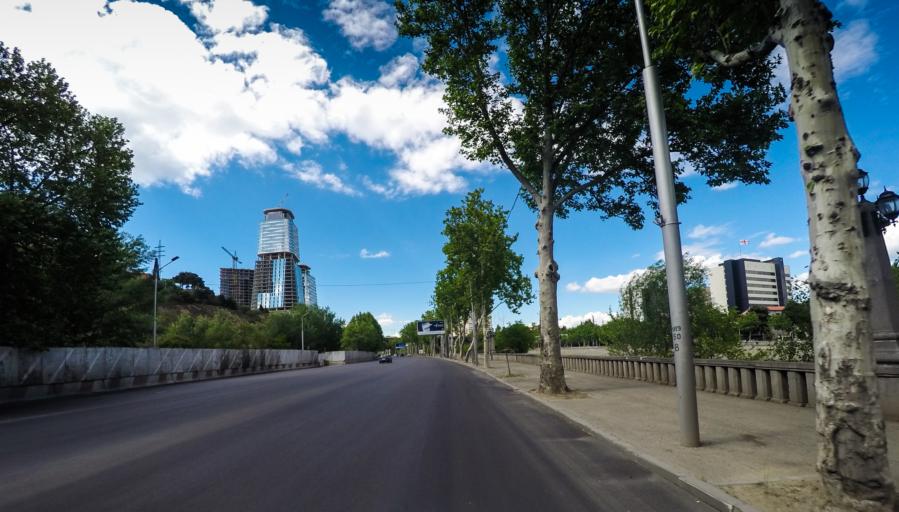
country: GE
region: T'bilisi
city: Tbilisi
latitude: 41.7140
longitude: 44.7883
